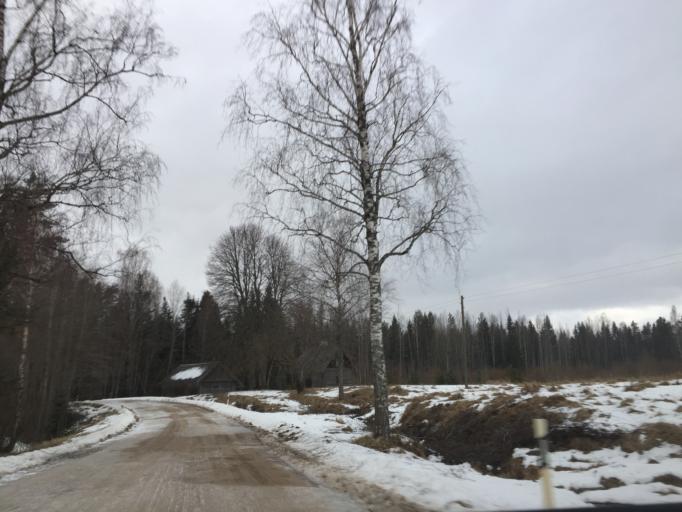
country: LV
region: Salacgrivas
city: Salacgriva
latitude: 57.6536
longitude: 24.4523
